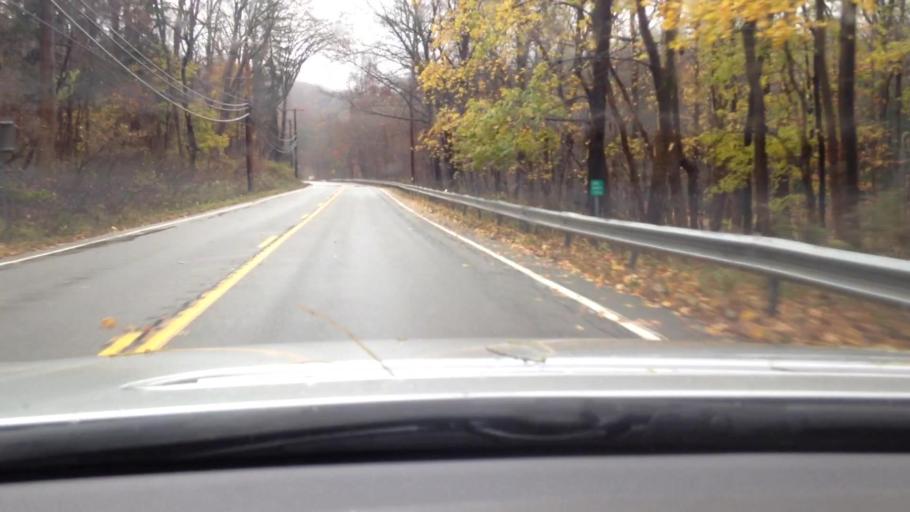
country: US
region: New York
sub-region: Orange County
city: West Point
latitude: 41.3656
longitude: -73.9279
